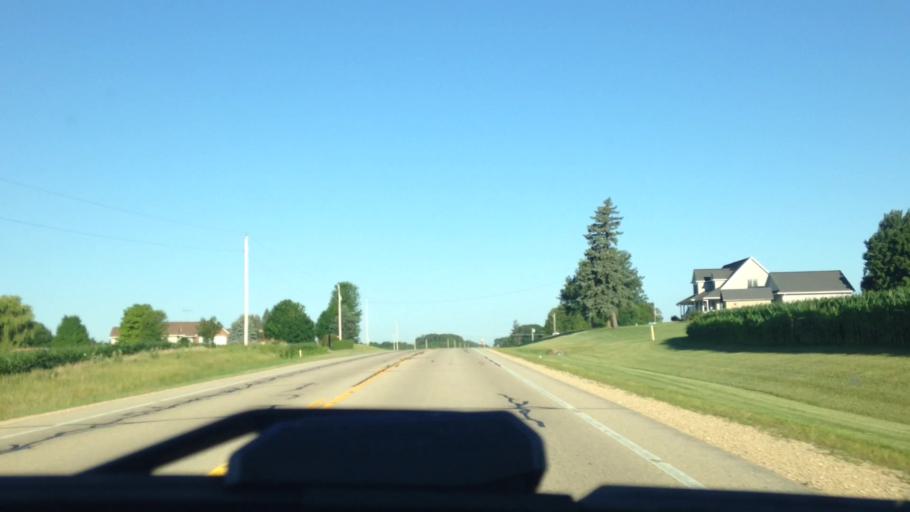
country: US
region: Wisconsin
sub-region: Columbia County
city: Fall River
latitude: 43.3411
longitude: -89.1031
